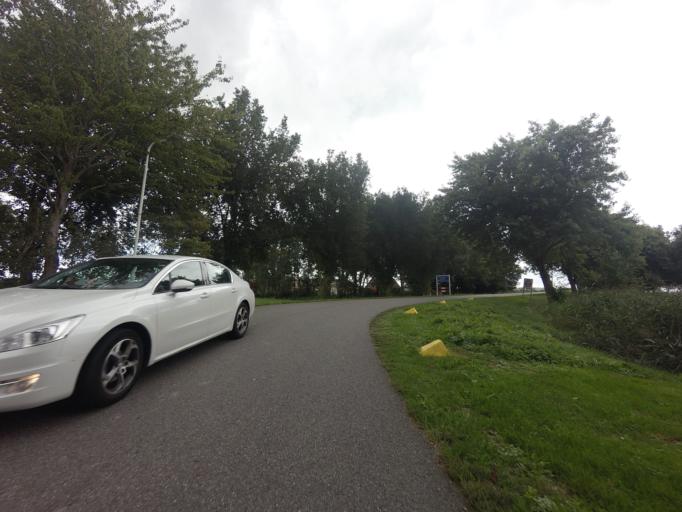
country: NL
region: Friesland
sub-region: Sudwest Fryslan
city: IJlst
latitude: 53.0072
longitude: 5.6339
